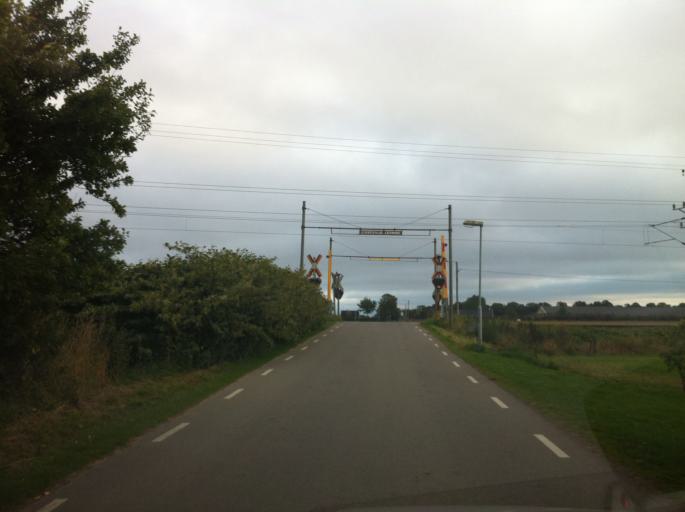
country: SE
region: Skane
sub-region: Helsingborg
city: Barslov
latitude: 56.0359
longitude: 12.8352
